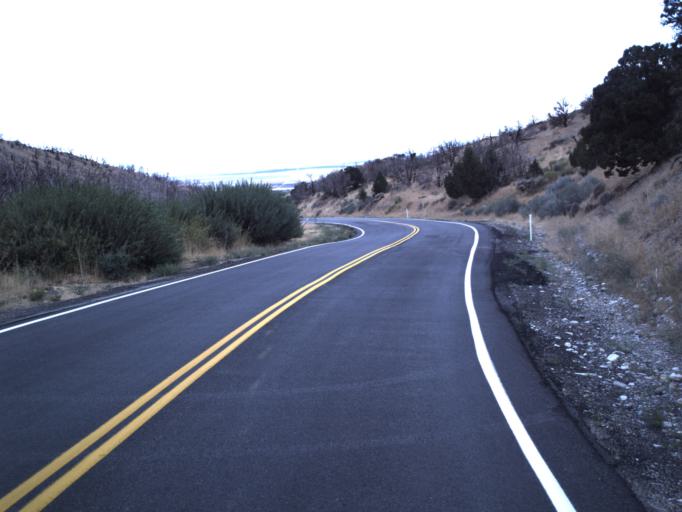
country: US
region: Utah
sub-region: Tooele County
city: Grantsville
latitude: 40.3369
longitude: -112.6130
